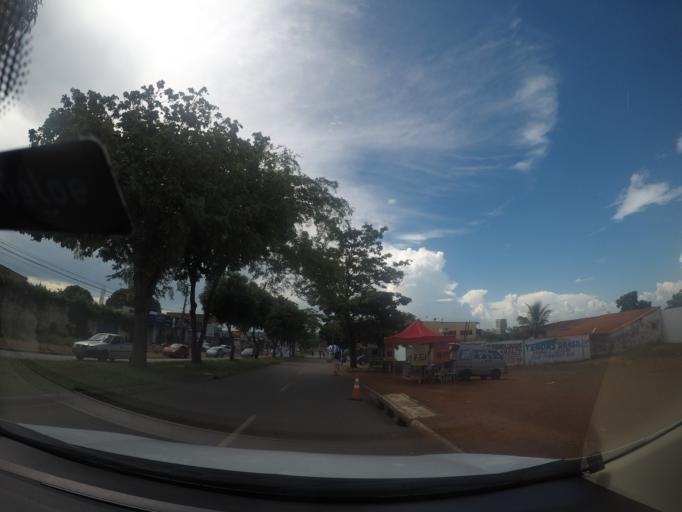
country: BR
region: Goias
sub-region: Trindade
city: Trindade
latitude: -16.6826
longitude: -49.3858
